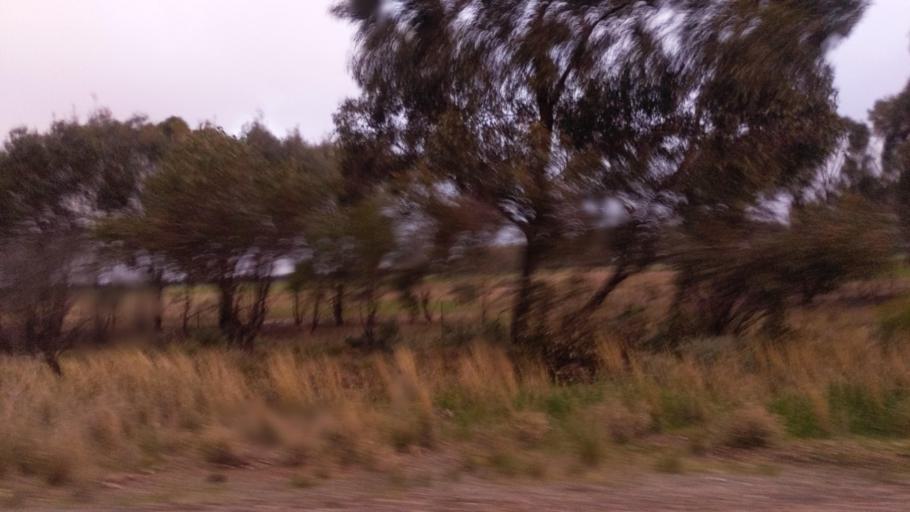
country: AU
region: New South Wales
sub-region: Coolamon
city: Coolamon
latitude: -34.7647
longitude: 146.9050
